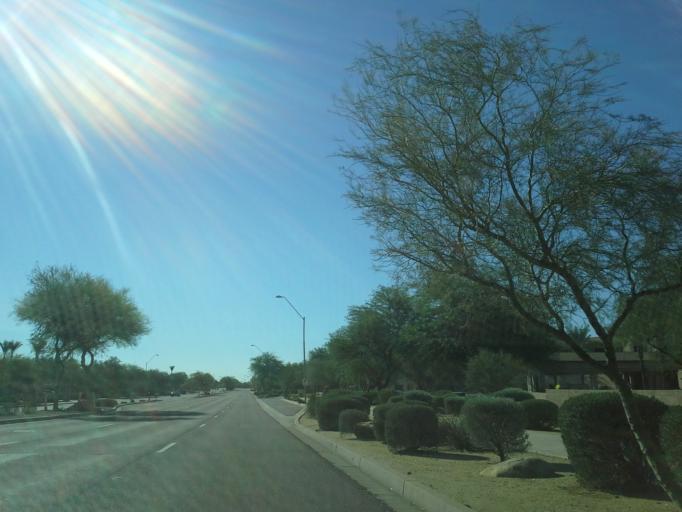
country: US
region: Arizona
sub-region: Maricopa County
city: Paradise Valley
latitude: 33.6190
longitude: -111.8732
